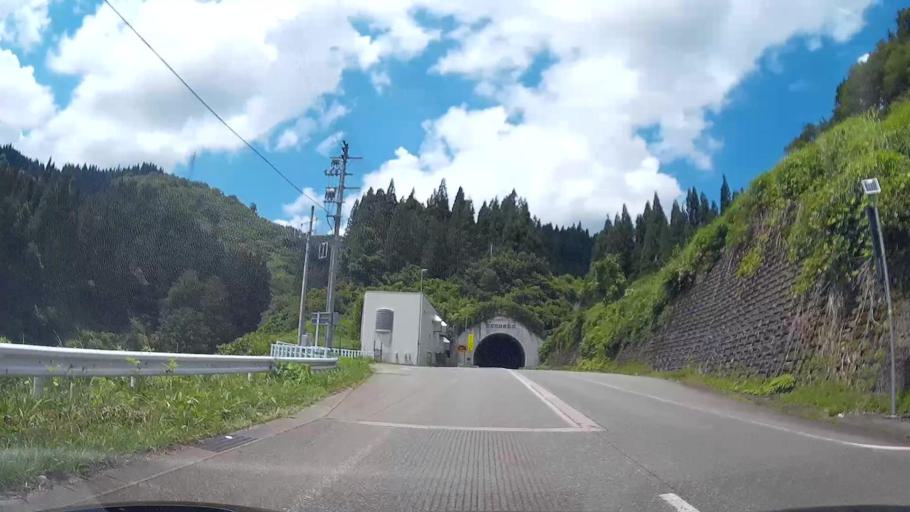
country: JP
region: Niigata
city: Shiozawa
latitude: 37.0232
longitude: 138.7995
